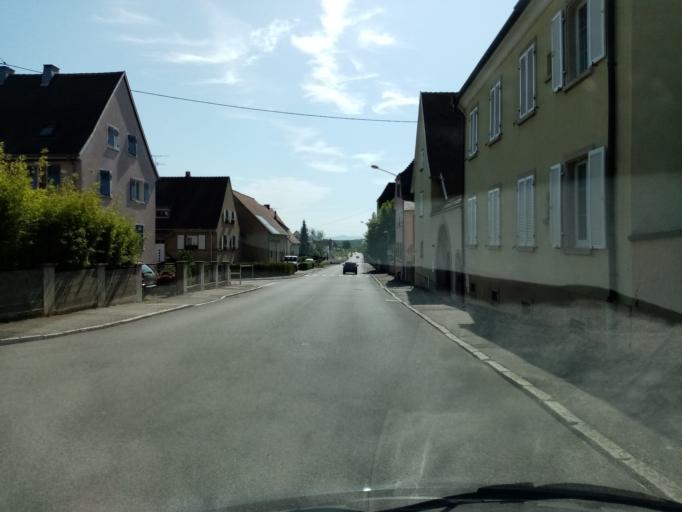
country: FR
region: Alsace
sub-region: Departement du Haut-Rhin
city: Bennwihr
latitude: 48.1428
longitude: 7.3252
